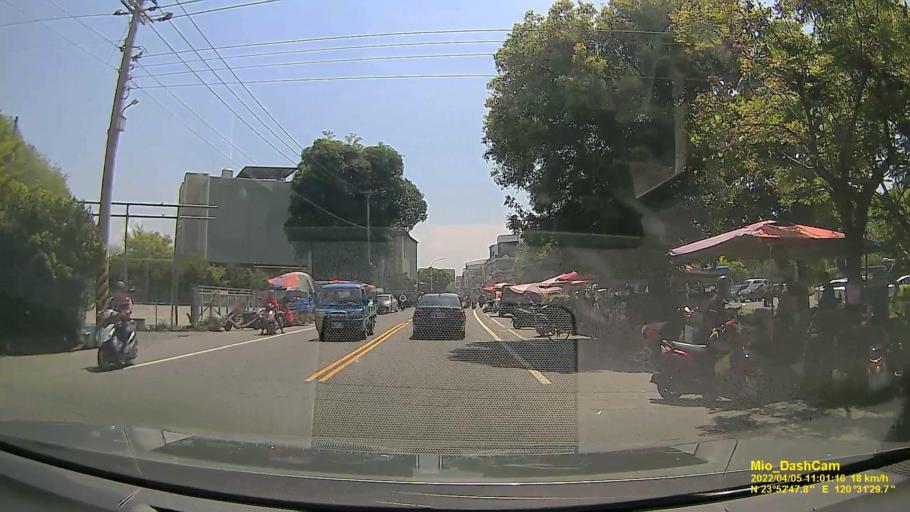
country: TW
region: Taiwan
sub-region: Nantou
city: Nantou
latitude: 23.8799
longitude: 120.5250
